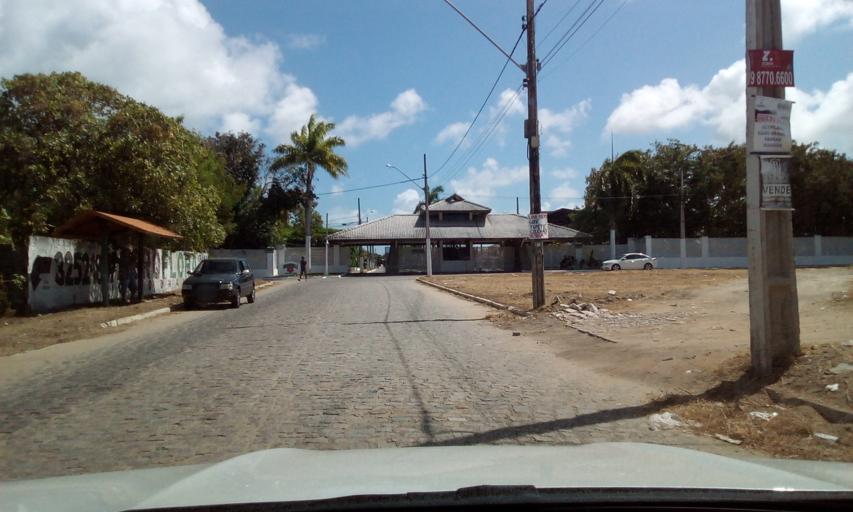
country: BR
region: Paraiba
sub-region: Joao Pessoa
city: Joao Pessoa
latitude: -7.1516
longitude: -34.8092
